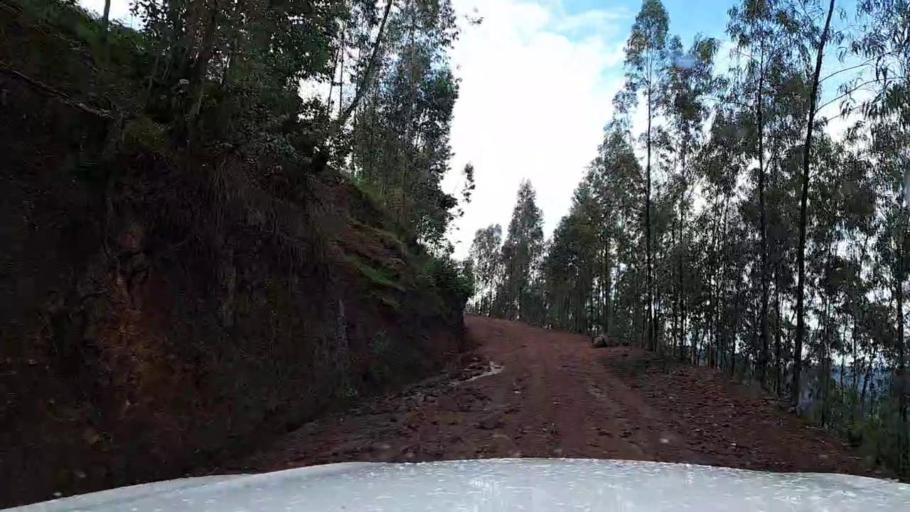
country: RW
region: Northern Province
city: Byumba
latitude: -1.7207
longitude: 29.9118
